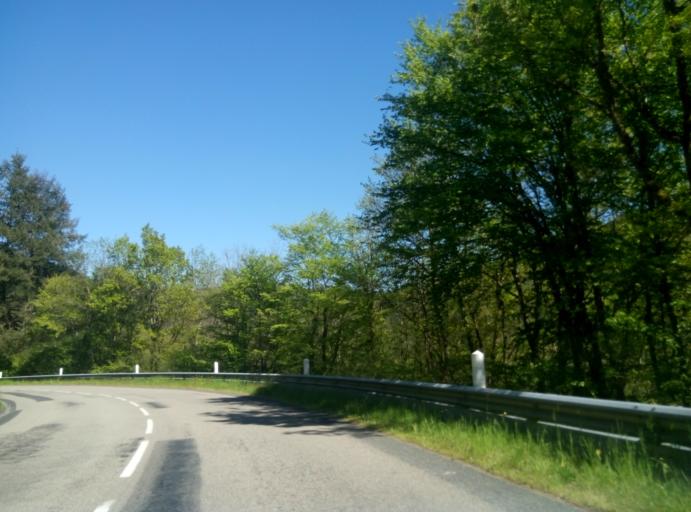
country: FR
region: Rhone-Alpes
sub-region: Departement du Rhone
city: Grandris
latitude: 46.0009
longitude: 4.4849
